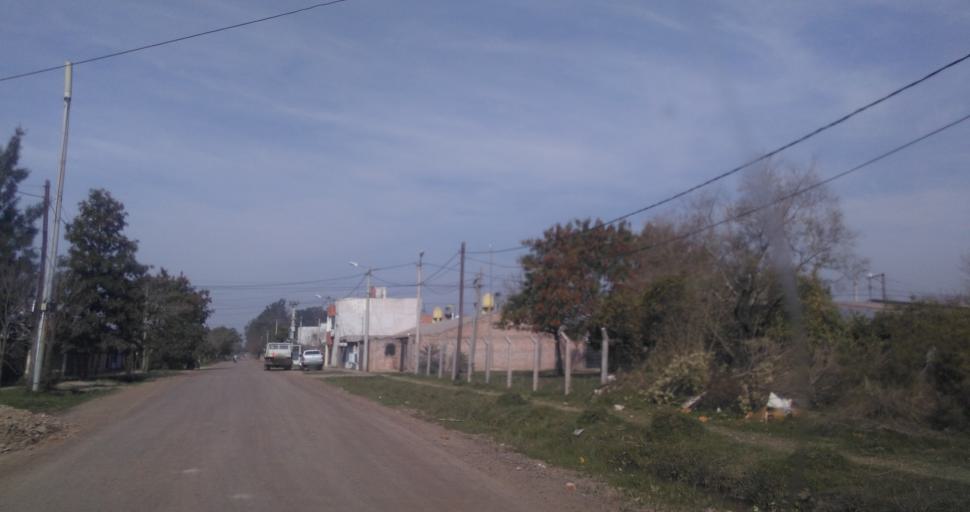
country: AR
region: Chaco
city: Fontana
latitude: -27.4426
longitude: -59.0320
